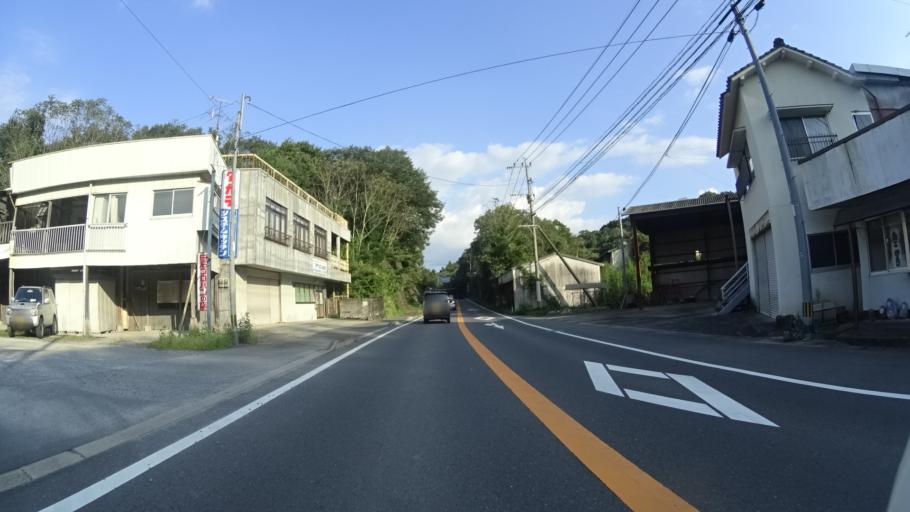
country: JP
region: Oita
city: Bungo-Takada-shi
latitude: 33.4445
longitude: 131.3445
